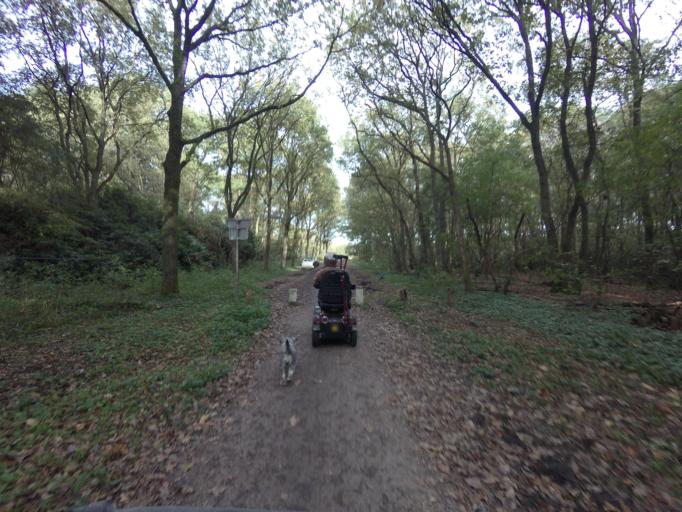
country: NL
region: North Holland
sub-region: Gemeente Laren
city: Laren
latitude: 52.2412
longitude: 5.2196
